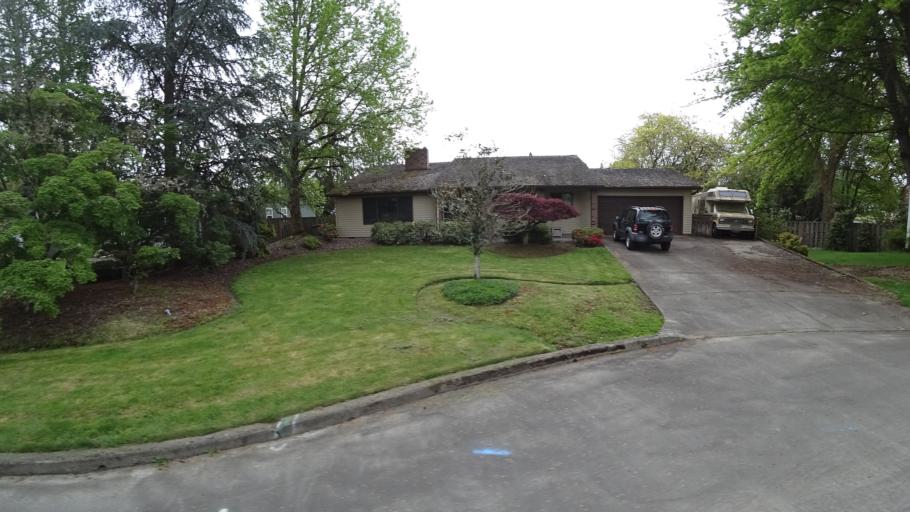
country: US
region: Oregon
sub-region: Washington County
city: Hillsboro
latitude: 45.5310
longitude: -122.9773
